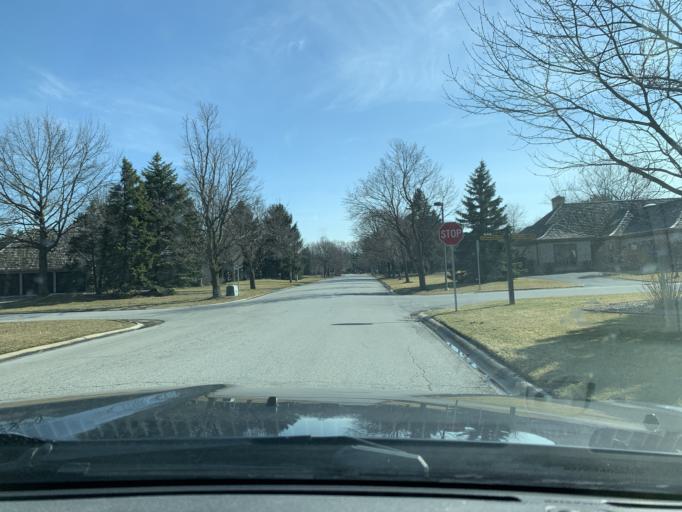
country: US
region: Indiana
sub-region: Lake County
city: Dyer
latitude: 41.5181
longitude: -87.4896
